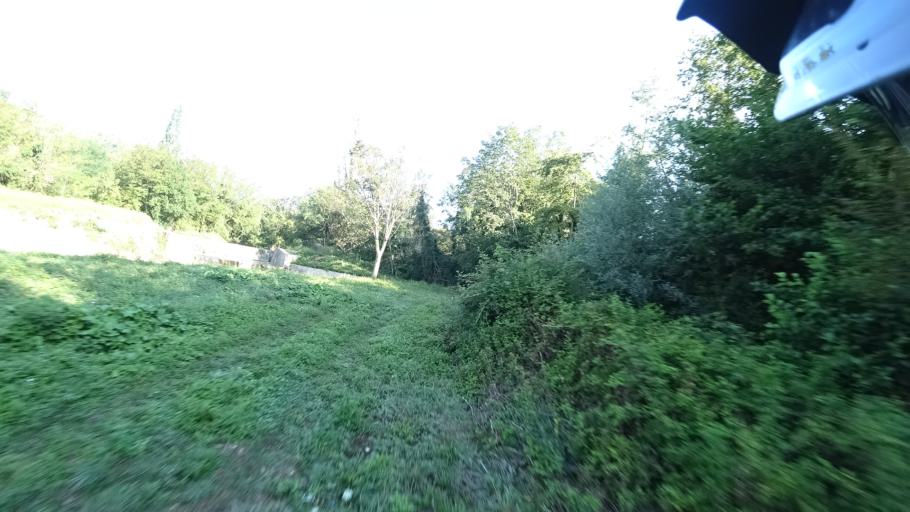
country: HR
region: Sibensko-Kniniska
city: Knin
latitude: 44.0760
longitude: 16.2063
